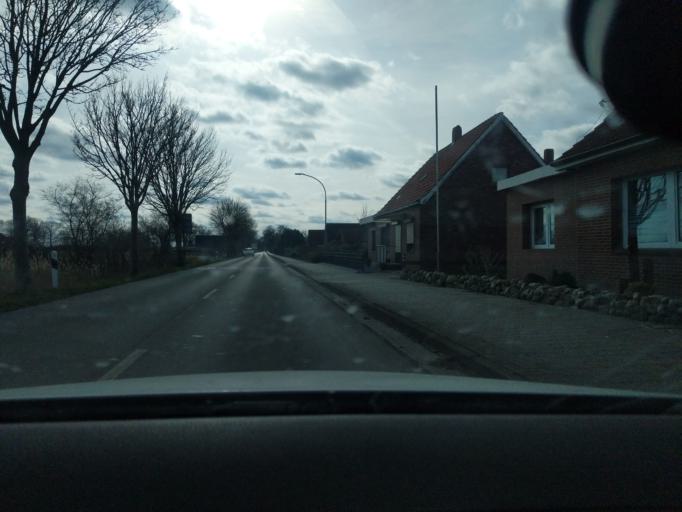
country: DE
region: Lower Saxony
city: Drochtersen
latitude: 53.6978
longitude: 9.4101
